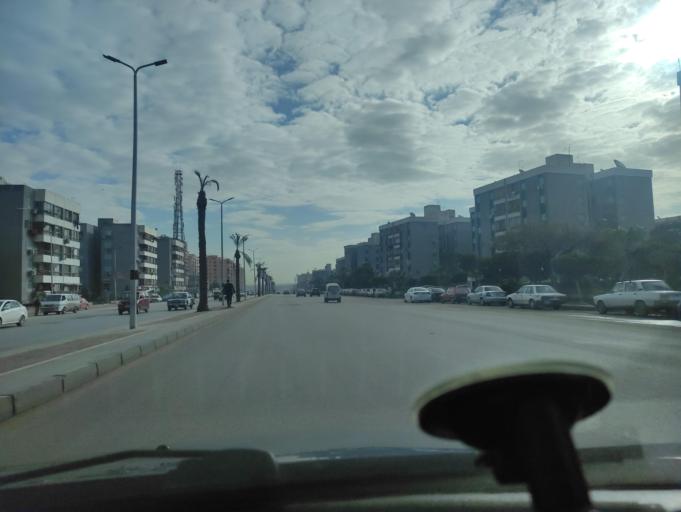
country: EG
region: Muhafazat al Qahirah
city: Cairo
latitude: 30.0502
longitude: 31.3903
